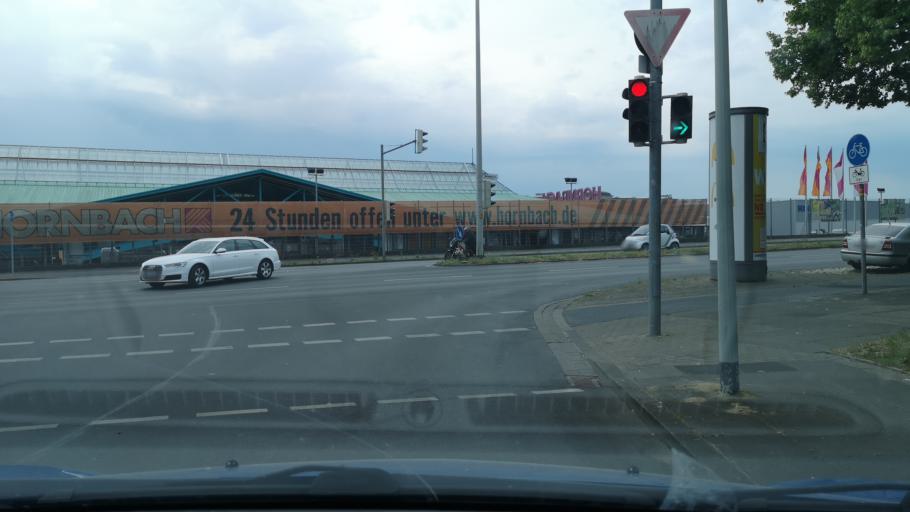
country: DE
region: Lower Saxony
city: Hannover
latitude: 52.3603
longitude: 9.7093
